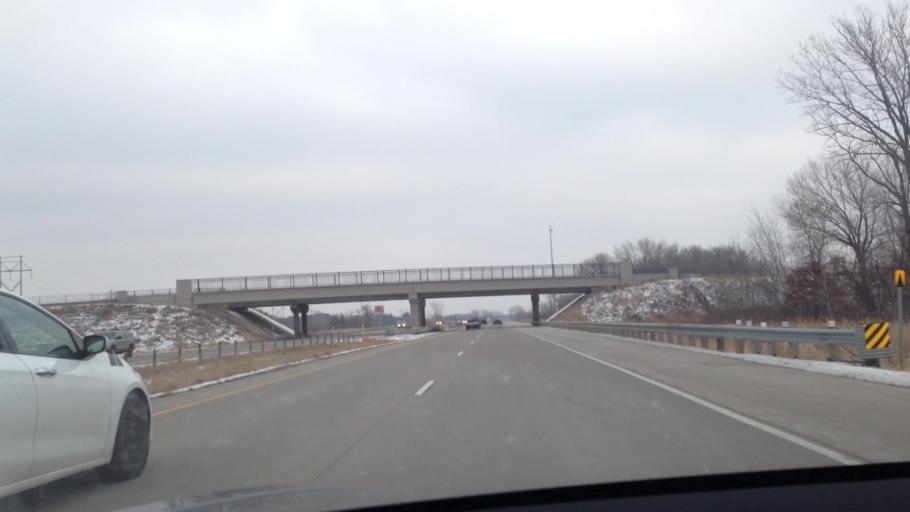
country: US
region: Minnesota
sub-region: Anoka County
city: Centerville
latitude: 45.1921
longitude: -93.0746
